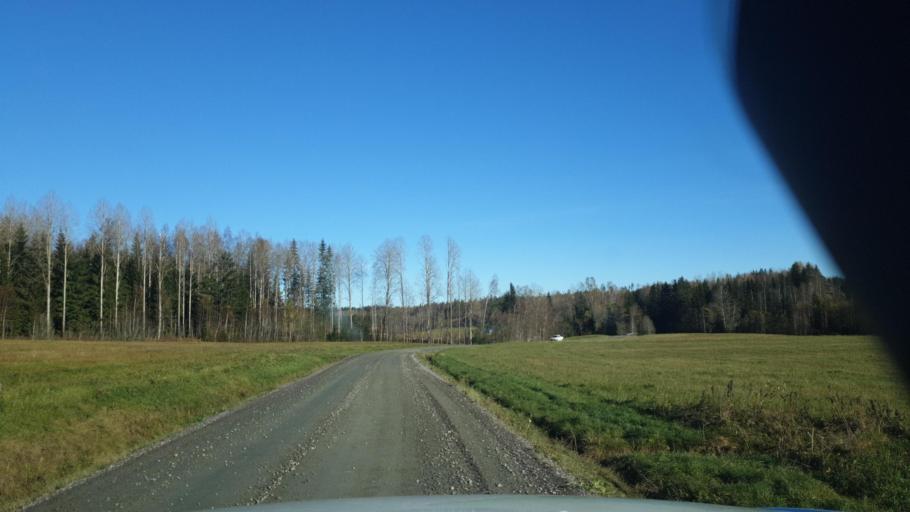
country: SE
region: Vaermland
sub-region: Karlstads Kommun
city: Edsvalla
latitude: 59.5010
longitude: 13.1900
